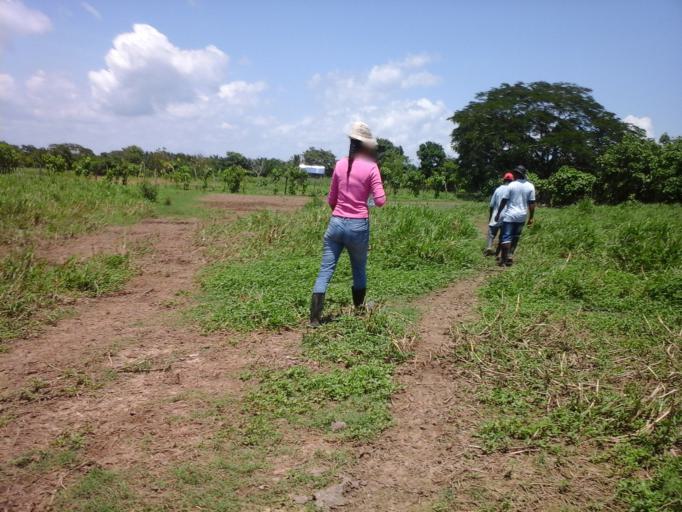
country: CO
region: Bolivar
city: Mahates
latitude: 10.1642
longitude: -75.2747
